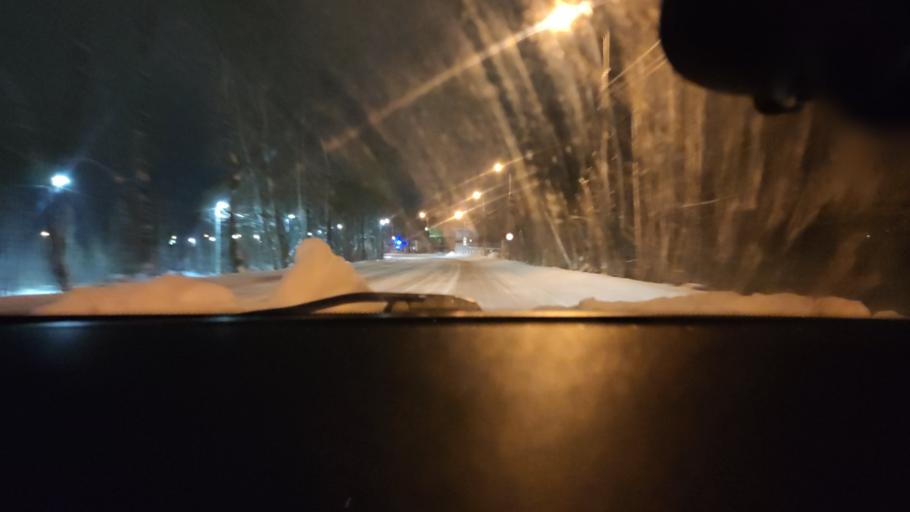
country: RU
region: Perm
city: Krasnokamsk
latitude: 58.0631
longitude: 55.8011
